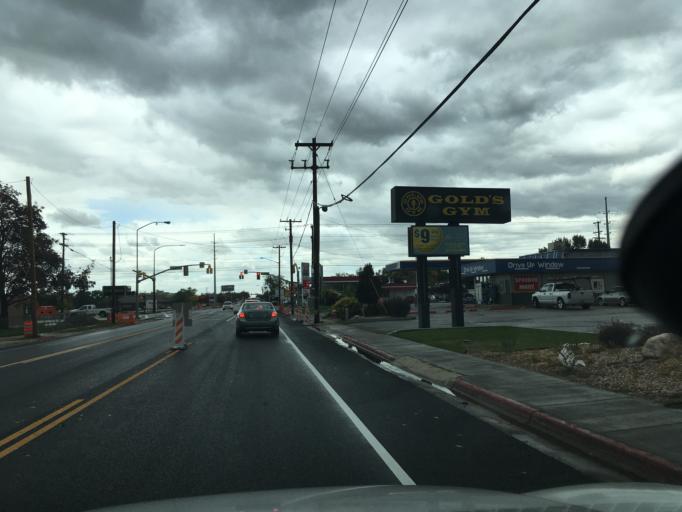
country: US
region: Utah
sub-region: Davis County
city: Layton
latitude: 41.0601
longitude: -111.9565
